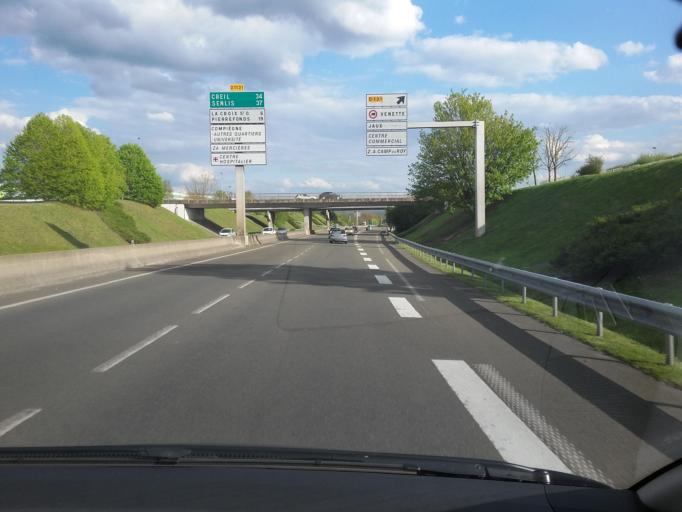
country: FR
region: Picardie
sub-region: Departement de l'Oise
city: Jaux
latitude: 49.4058
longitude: 2.7800
